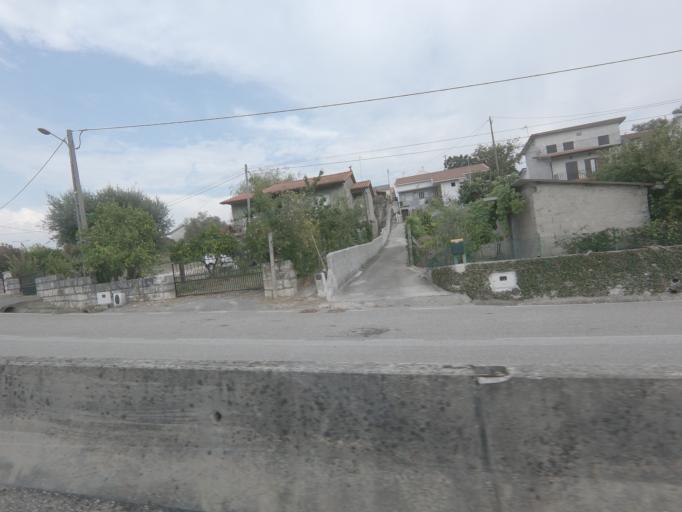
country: PT
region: Aveiro
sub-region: Mealhada
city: Pampilhosa do Botao
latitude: 40.2719
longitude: -8.4435
